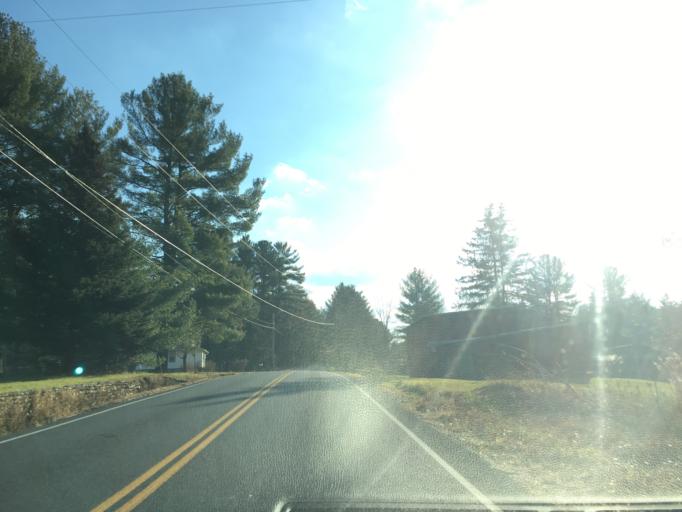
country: US
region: New York
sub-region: Rensselaer County
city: West Sand Lake
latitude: 42.6005
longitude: -73.6001
